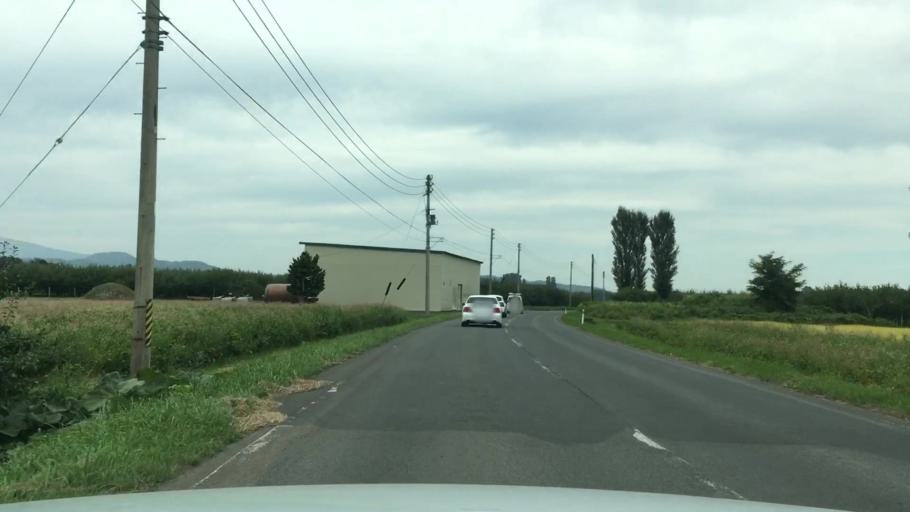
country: JP
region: Aomori
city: Hirosaki
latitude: 40.6458
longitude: 140.4245
